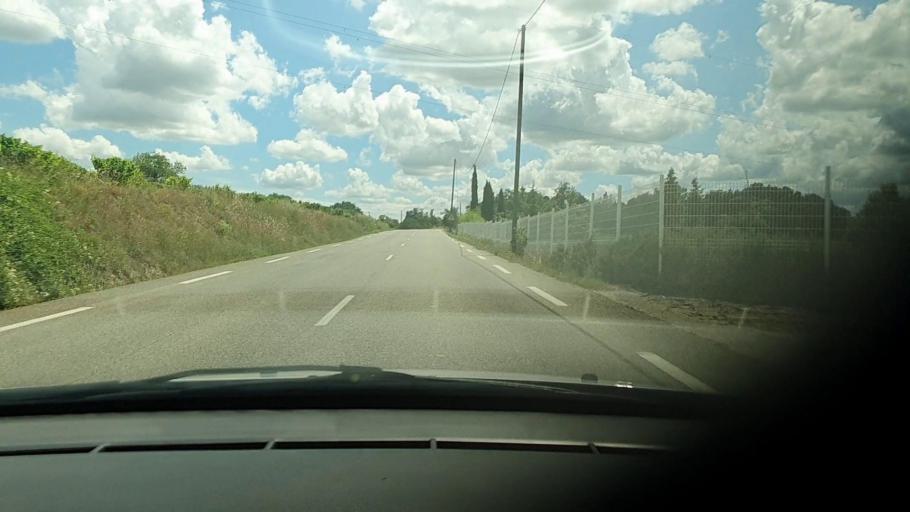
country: FR
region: Languedoc-Roussillon
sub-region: Departement du Gard
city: Mons
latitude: 44.0586
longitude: 4.2221
